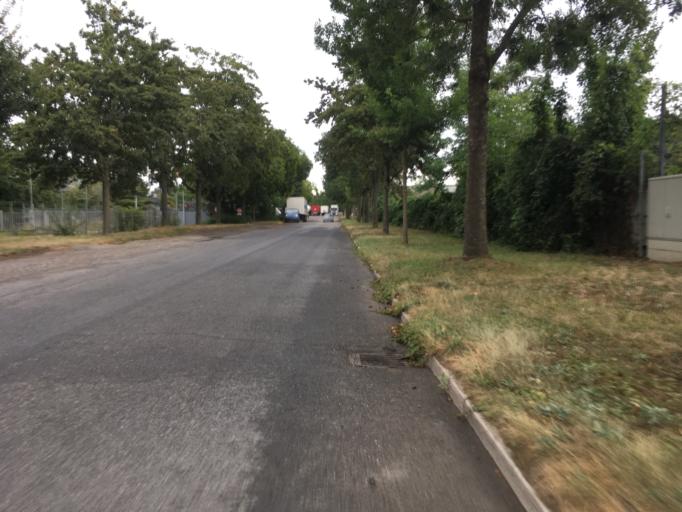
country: DE
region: Baden-Wuerttemberg
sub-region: Regierungsbezirk Stuttgart
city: Neckarsulm
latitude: 49.1793
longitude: 9.2092
